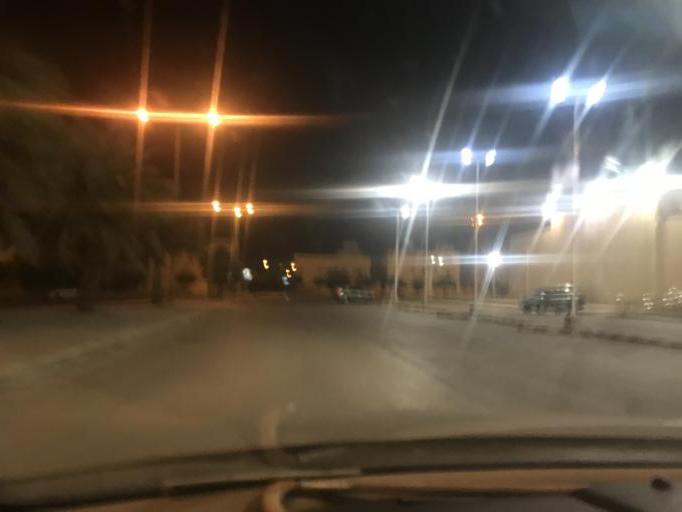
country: SA
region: Ar Riyad
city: Riyadh
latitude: 24.6757
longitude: 46.7806
